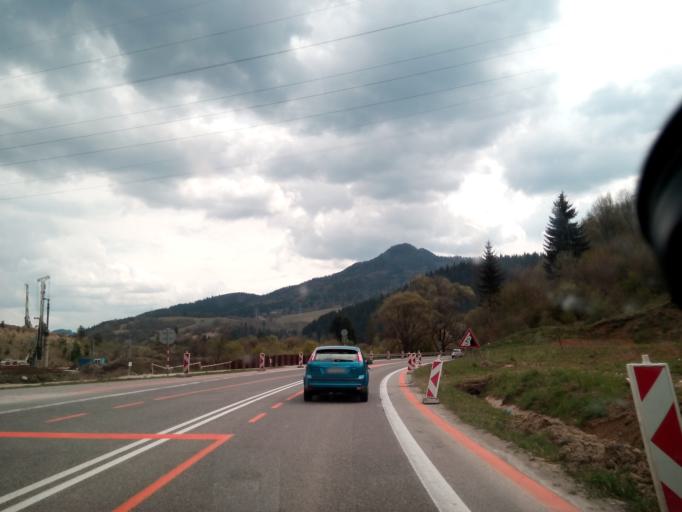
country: SK
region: Zilinsky
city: Ruzomberok
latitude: 49.1176
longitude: 19.2265
